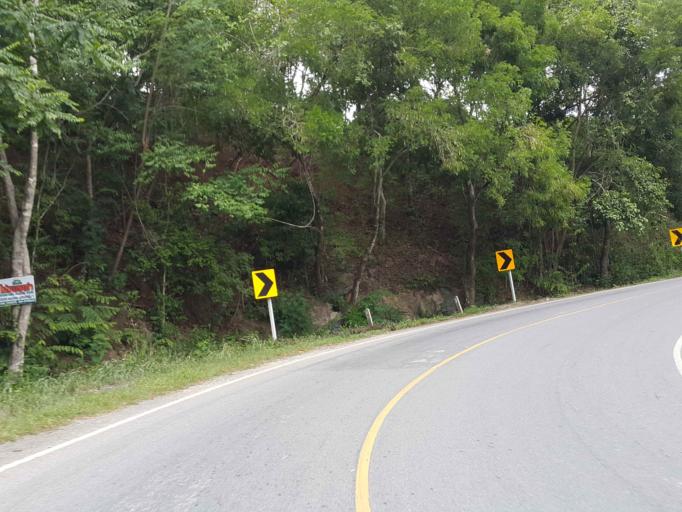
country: TH
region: Chiang Mai
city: Hang Dong
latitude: 18.7546
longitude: 98.8827
